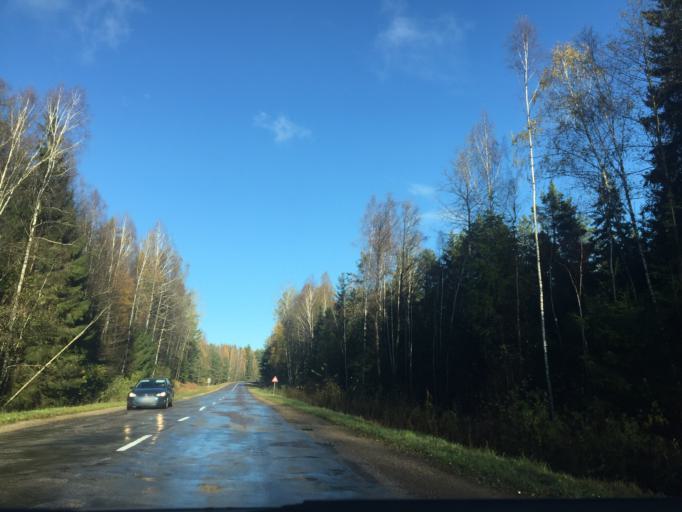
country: LV
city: Tireli
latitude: 56.8783
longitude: 23.5375
